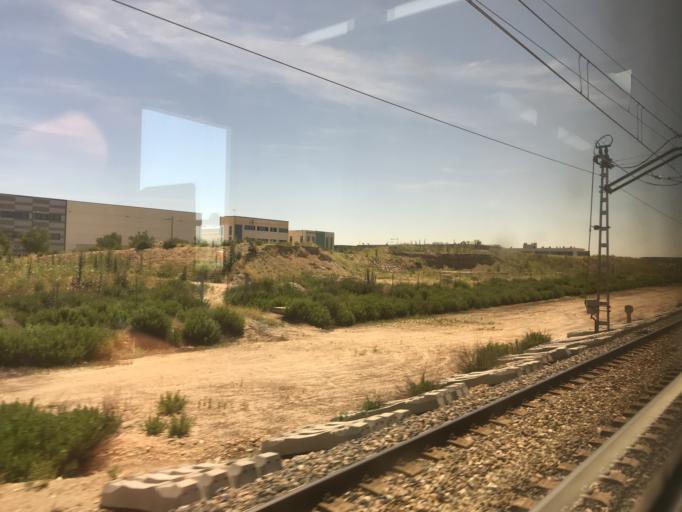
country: ES
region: Madrid
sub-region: Provincia de Madrid
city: Getafe
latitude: 40.2945
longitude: -3.7059
